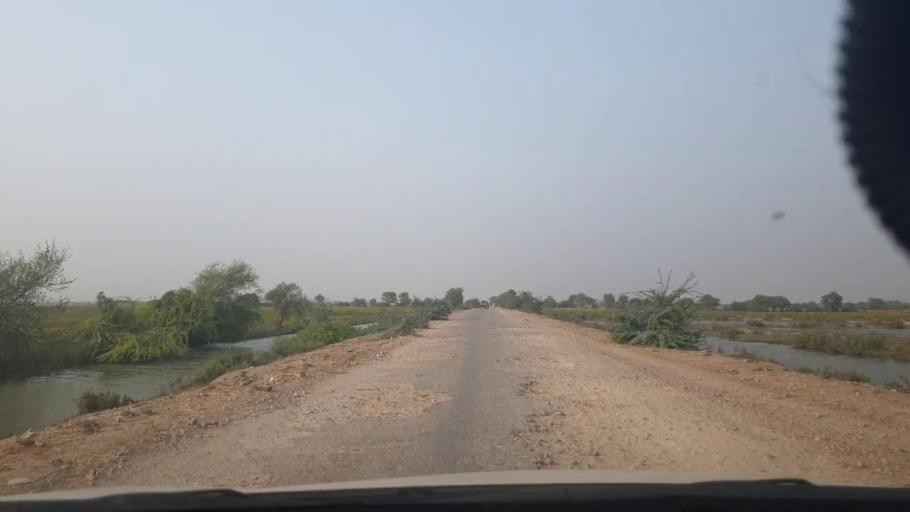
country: PK
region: Sindh
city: Bulri
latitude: 24.7798
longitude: 68.4198
